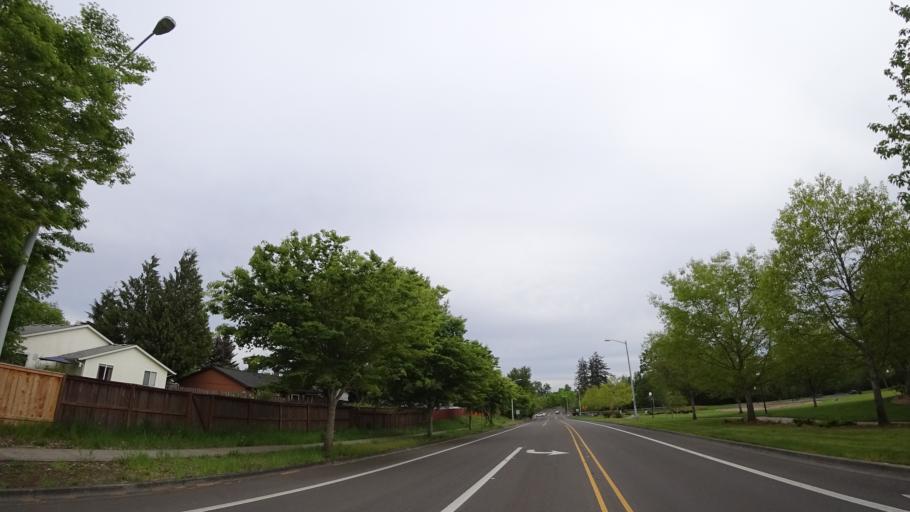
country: US
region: Oregon
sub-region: Washington County
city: Aloha
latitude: 45.5104
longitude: -122.9162
